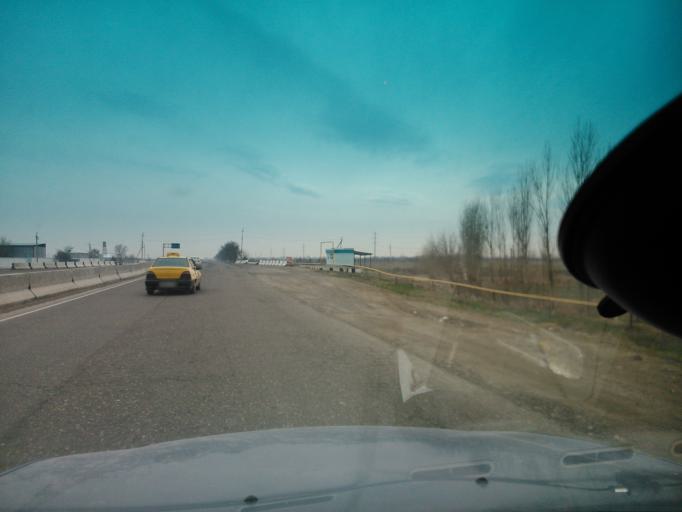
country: UZ
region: Sirdaryo
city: Guliston
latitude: 40.4349
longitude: 68.7801
